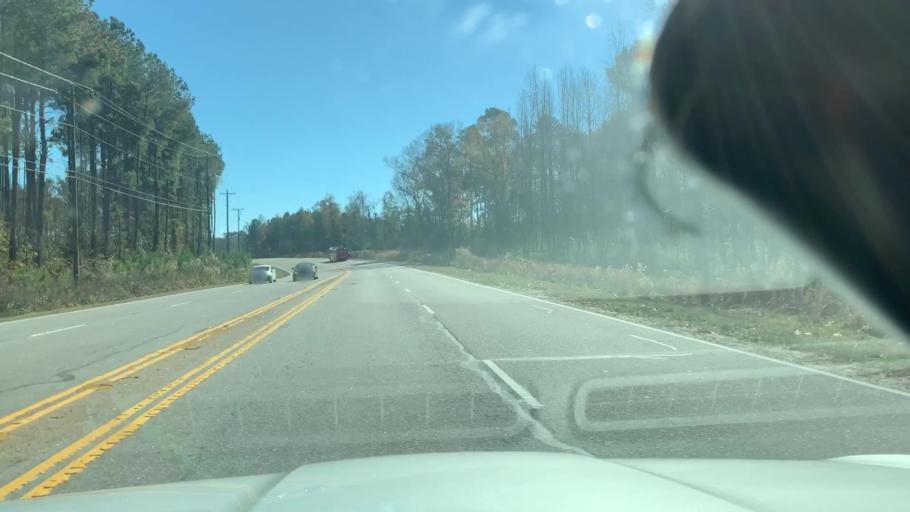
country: US
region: South Carolina
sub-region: Richland County
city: Columbia
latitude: 33.9417
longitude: -80.9846
